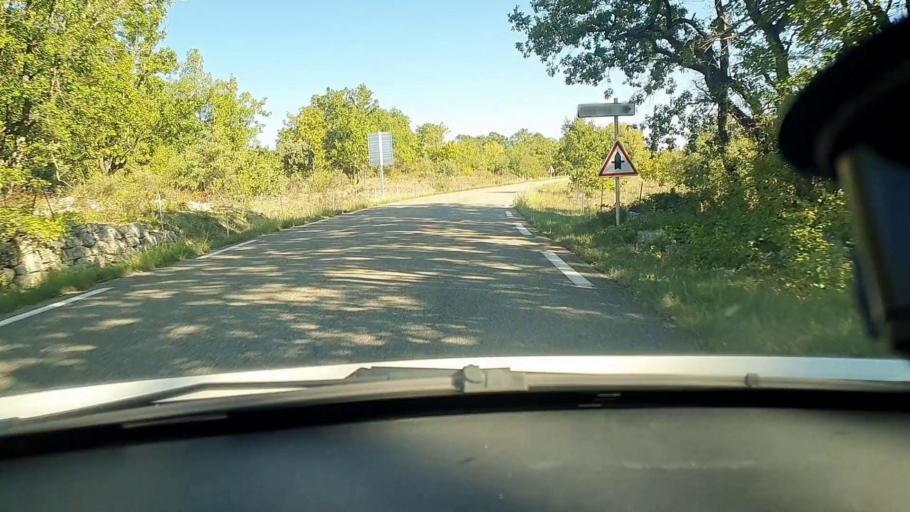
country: FR
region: Languedoc-Roussillon
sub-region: Departement du Gard
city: Goudargues
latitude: 44.2878
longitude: 4.4678
